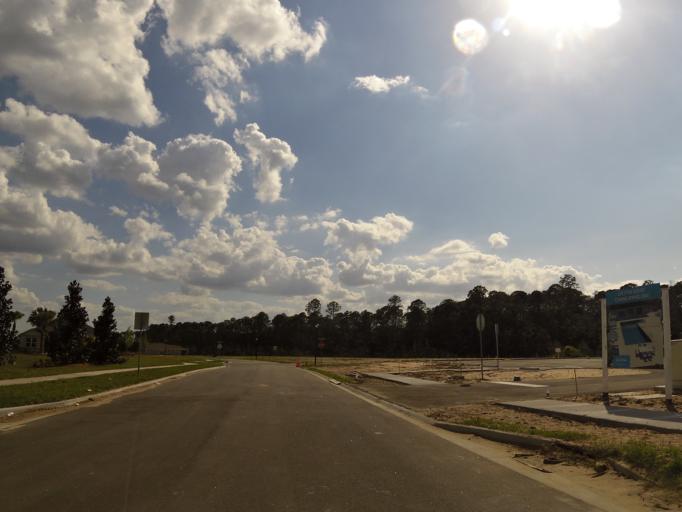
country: US
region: Florida
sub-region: Saint Johns County
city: Palm Valley
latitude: 30.1749
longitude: -81.5098
